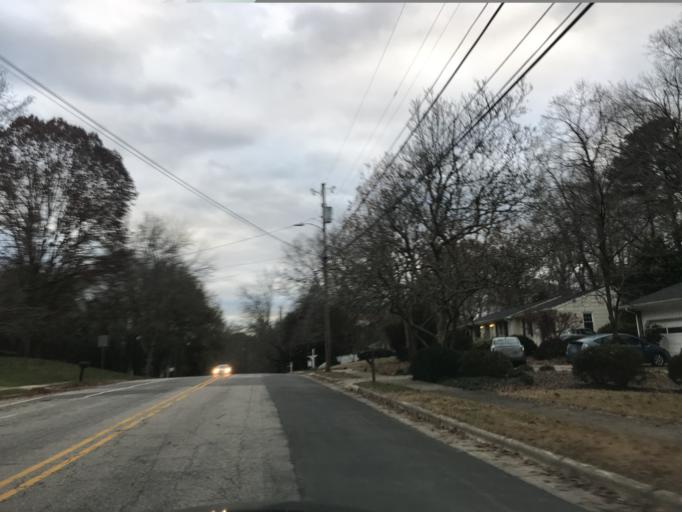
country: US
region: North Carolina
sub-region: Wake County
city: West Raleigh
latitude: 35.8466
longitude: -78.6603
